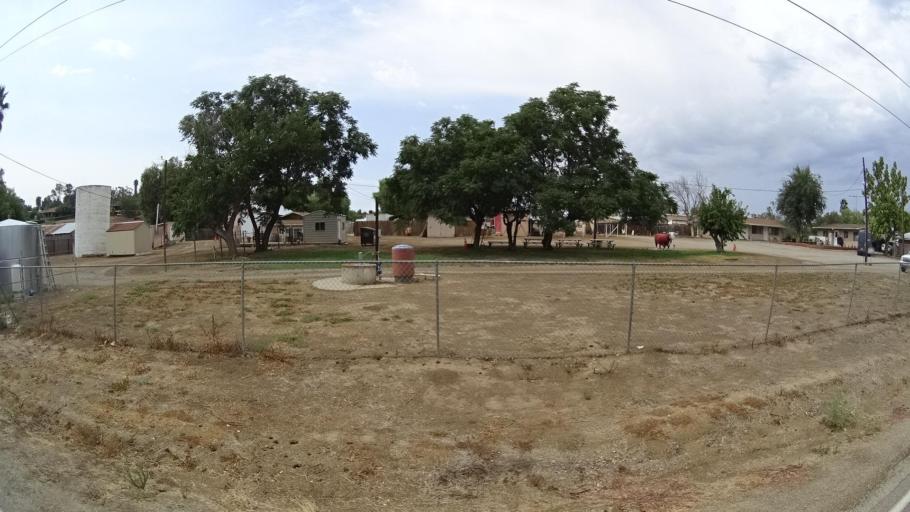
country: US
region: California
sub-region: San Diego County
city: Ramona
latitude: 33.0607
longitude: -116.8608
